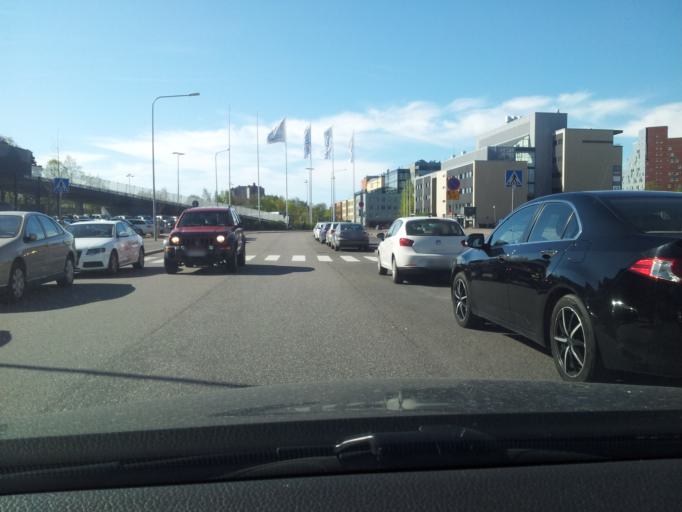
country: FI
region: Uusimaa
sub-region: Helsinki
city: Helsinki
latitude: 60.2066
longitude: 24.9009
